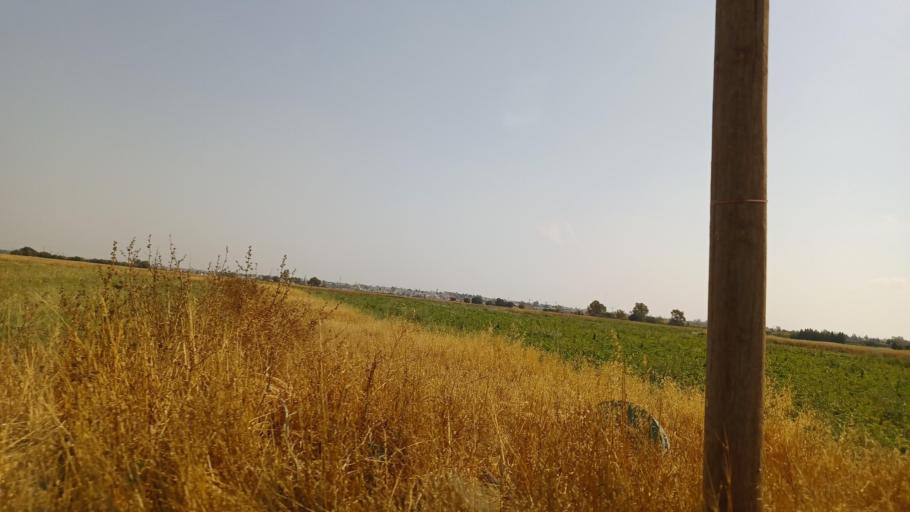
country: CY
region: Ammochostos
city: Avgorou
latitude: 35.0578
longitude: 33.8707
